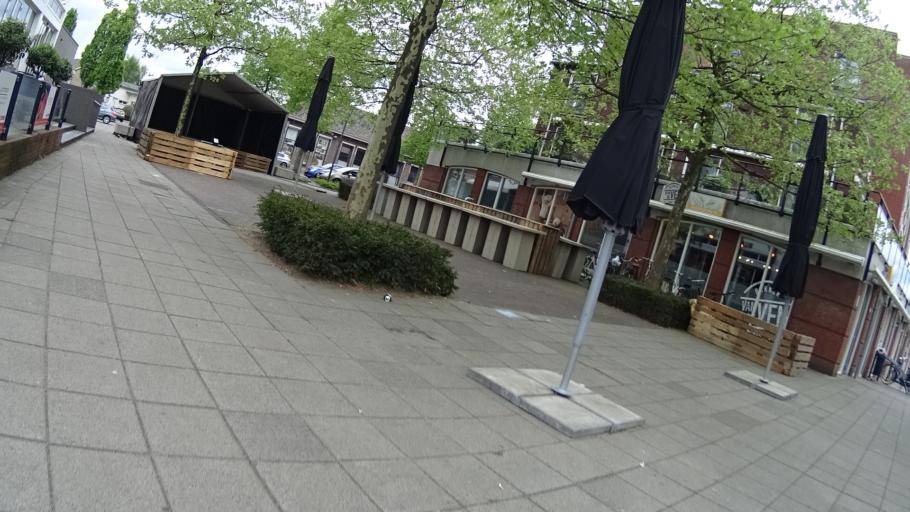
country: NL
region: North Brabant
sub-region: Gemeente Boekel
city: Boekel
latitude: 51.6029
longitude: 5.6720
